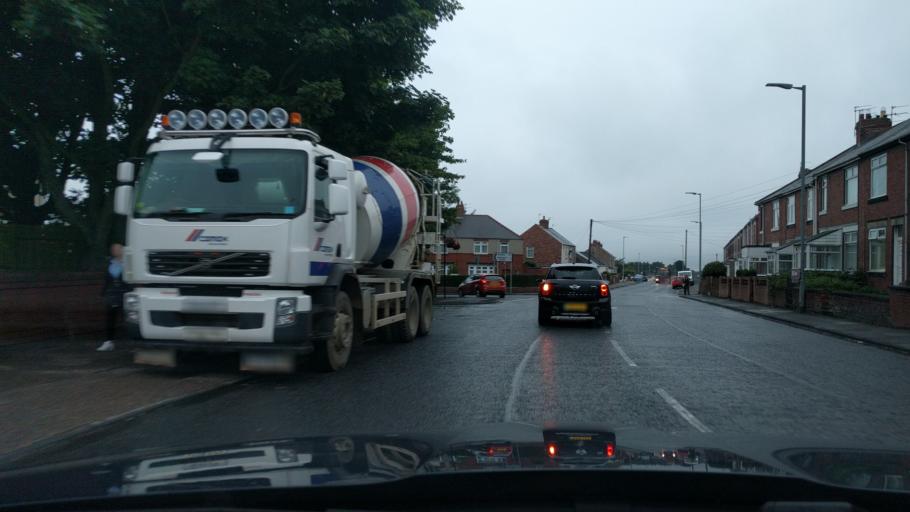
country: GB
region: England
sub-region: Northumberland
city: Bedlington
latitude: 55.1332
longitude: -1.5845
